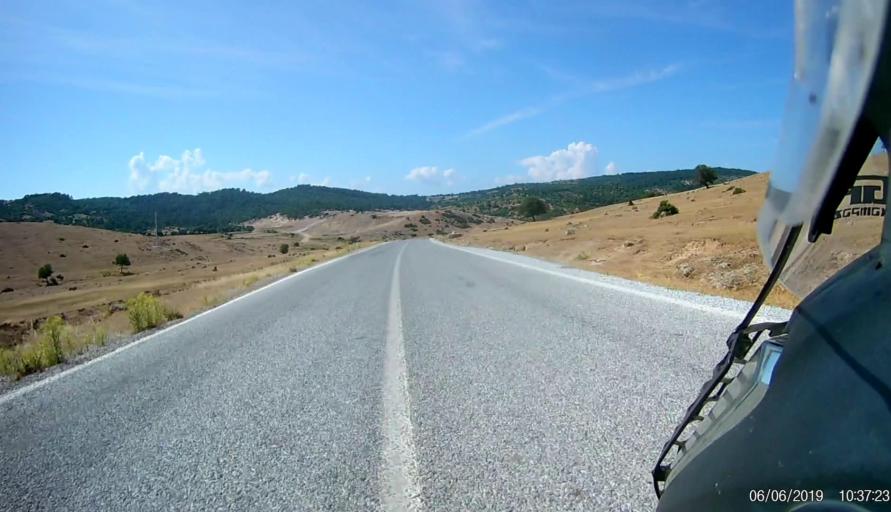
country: TR
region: Canakkale
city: Ayvacik
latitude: 39.5242
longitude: 26.4708
